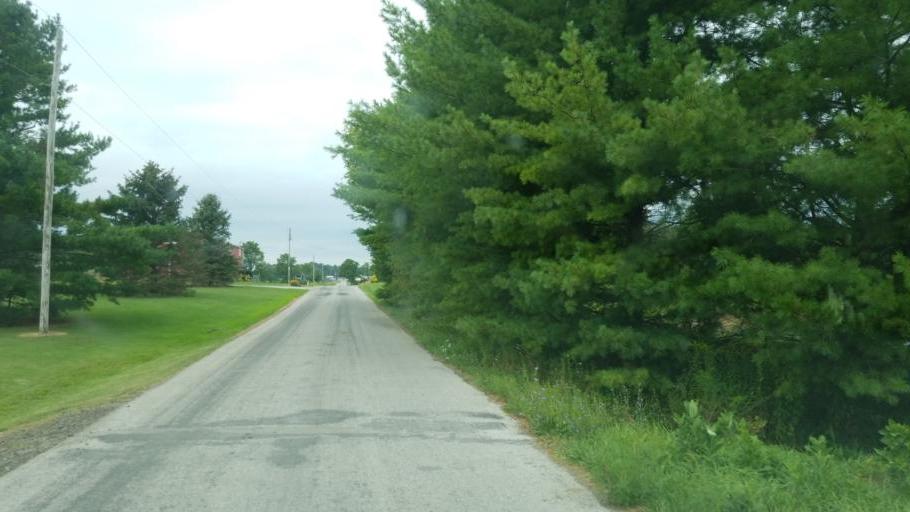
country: US
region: Ohio
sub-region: Morrow County
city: Mount Gilead
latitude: 40.5181
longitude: -82.8045
